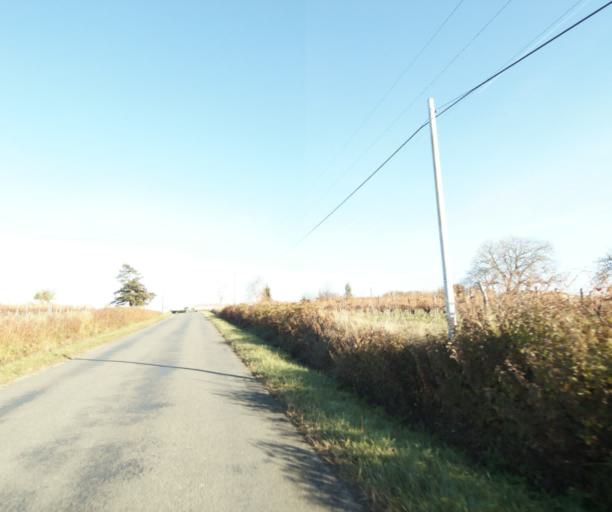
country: FR
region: Poitou-Charentes
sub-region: Departement de la Charente-Maritime
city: Cherac
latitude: 45.7368
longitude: -0.4503
